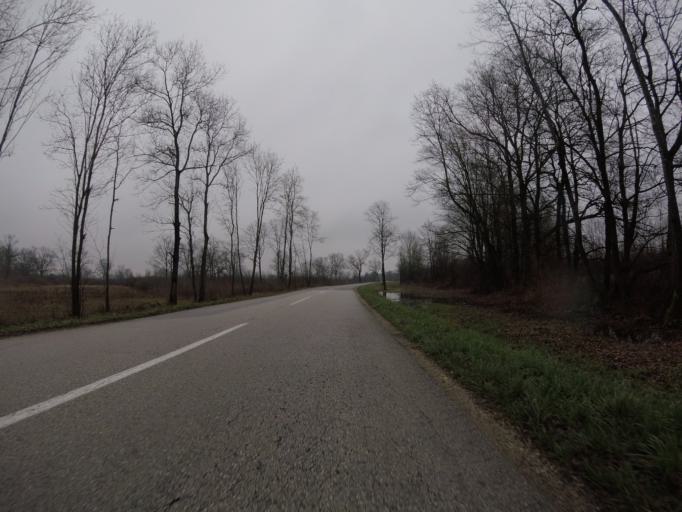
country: HR
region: Zagrebacka
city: Kuce
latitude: 45.7065
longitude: 16.1881
